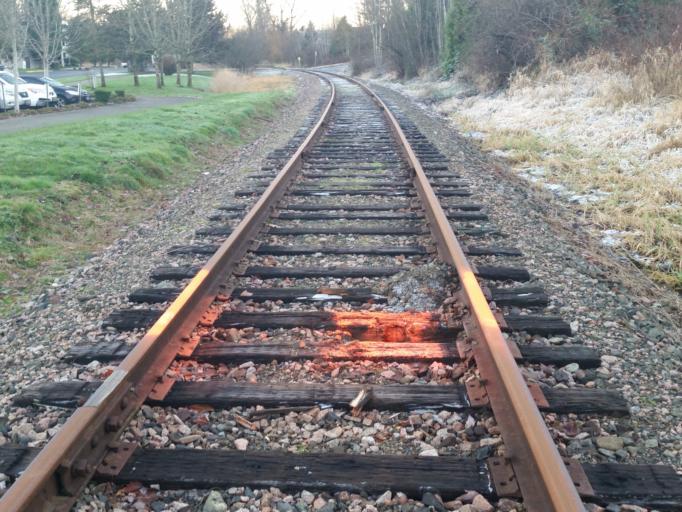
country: US
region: Washington
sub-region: King County
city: Woodinville
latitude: 47.7378
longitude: -122.1554
